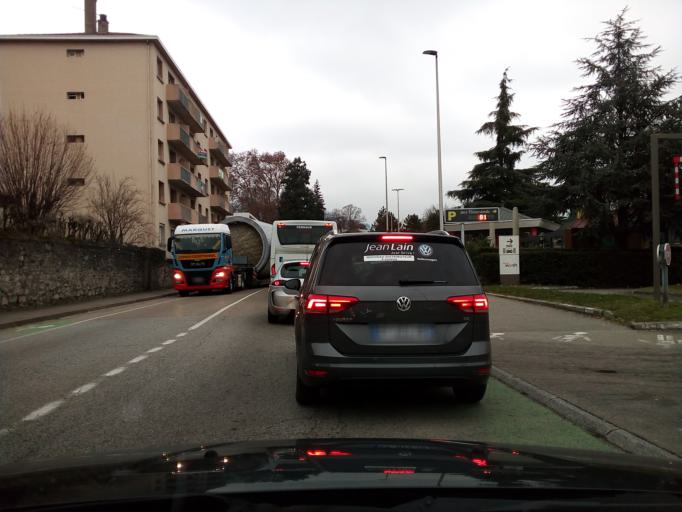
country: FR
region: Rhone-Alpes
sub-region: Departement de l'Isere
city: Voiron
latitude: 45.3587
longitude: 5.5919
